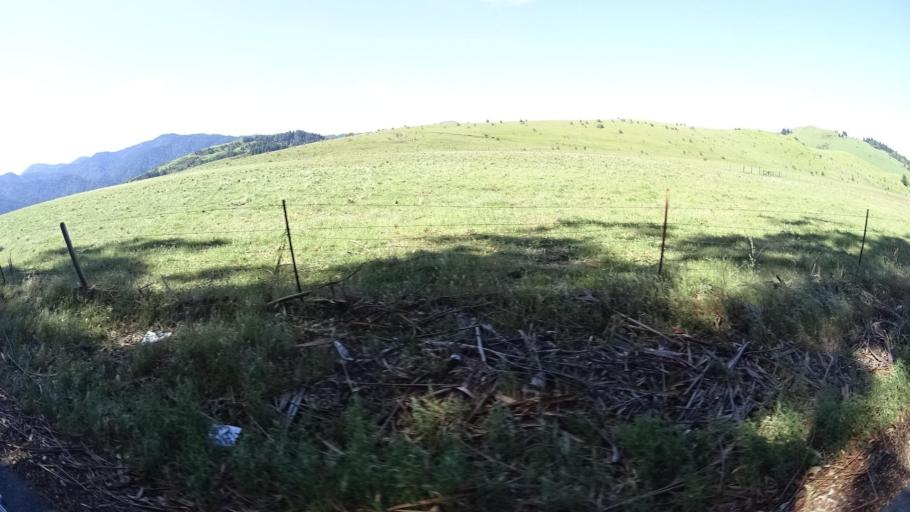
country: US
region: California
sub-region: Humboldt County
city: Ferndale
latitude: 40.3363
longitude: -124.3086
